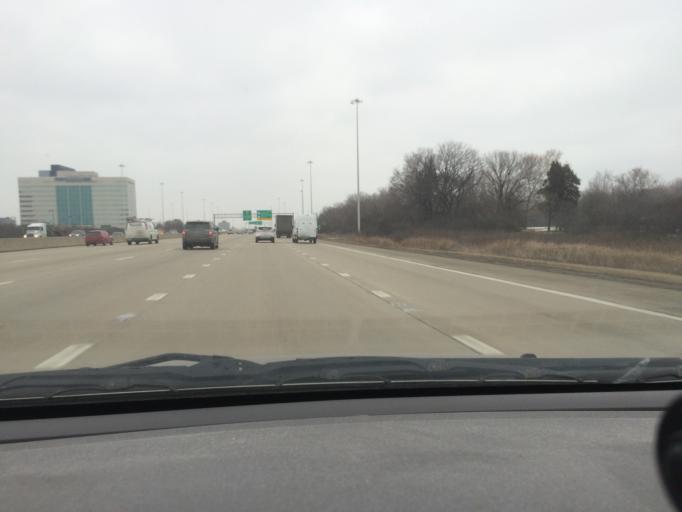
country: US
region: Illinois
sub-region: Cook County
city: Hoffman Estates
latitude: 42.0284
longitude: -88.0308
